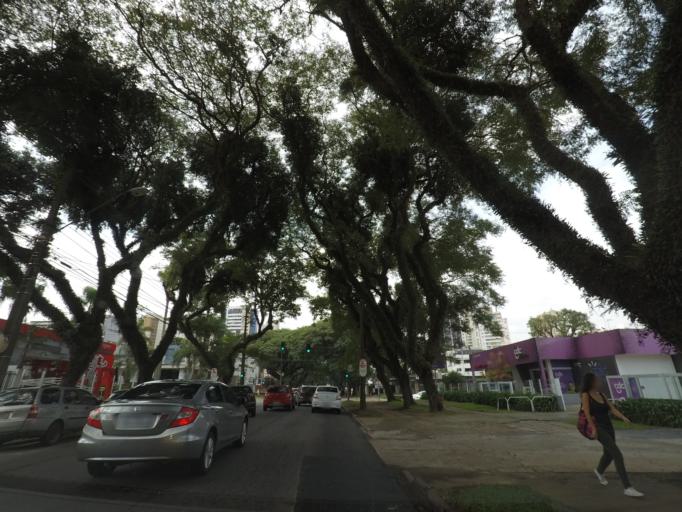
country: BR
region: Parana
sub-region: Curitiba
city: Curitiba
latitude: -25.4528
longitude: -49.2925
